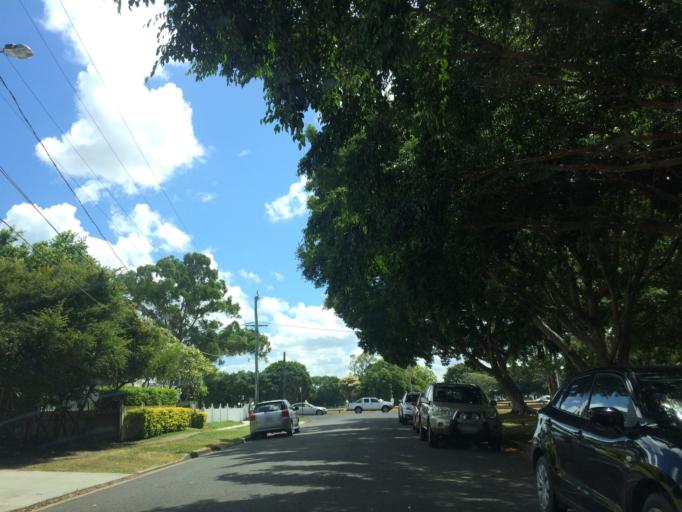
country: AU
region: Queensland
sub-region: Brisbane
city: Seven Hills
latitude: -27.4834
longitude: 153.0630
